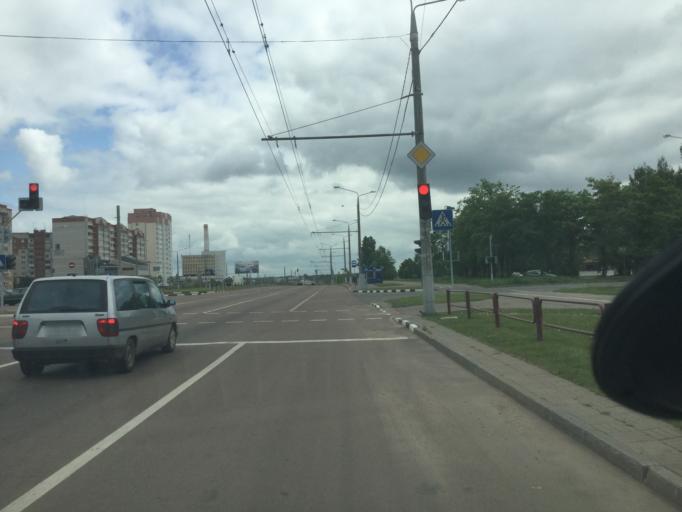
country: BY
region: Vitebsk
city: Vitebsk
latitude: 55.1602
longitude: 30.2264
